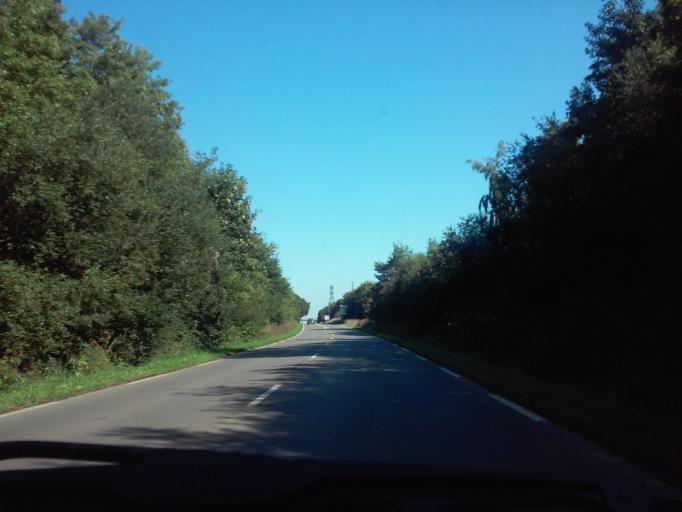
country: FR
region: Brittany
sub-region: Departement d'Ille-et-Vilaine
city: Betton
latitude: 48.1553
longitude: -1.6513
